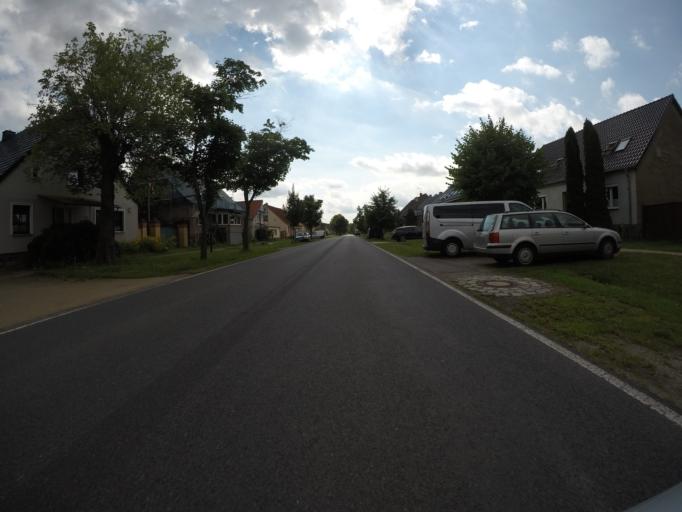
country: DE
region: Brandenburg
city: Grosswoltersdorf
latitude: 53.0701
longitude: 13.0949
